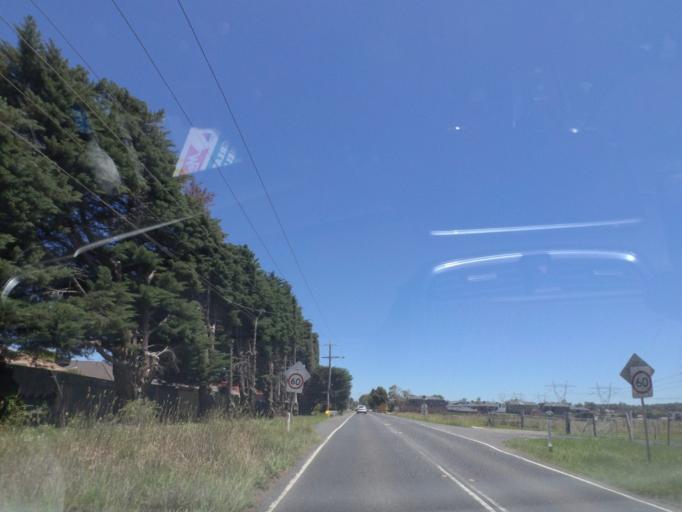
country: AU
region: Victoria
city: Plenty
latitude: -37.6524
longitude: 145.0993
